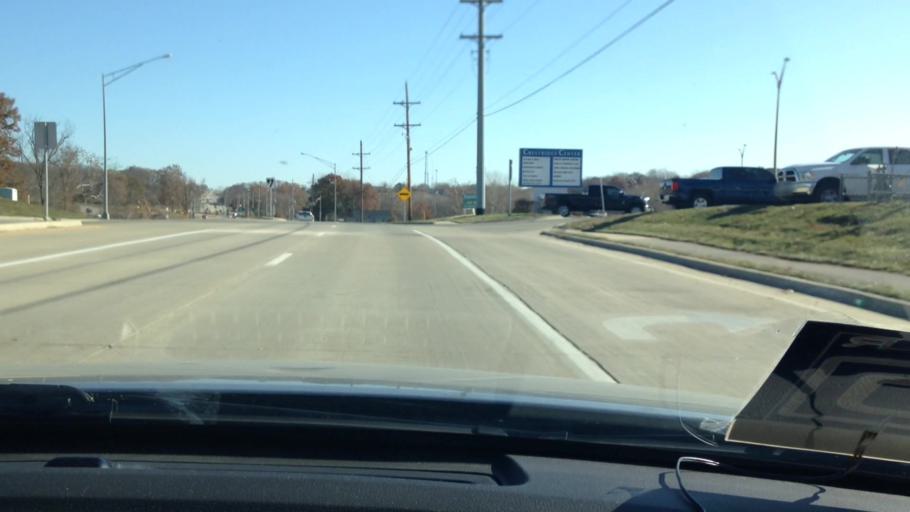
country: US
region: Missouri
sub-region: Platte County
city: Parkville
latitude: 39.2098
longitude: -94.7089
